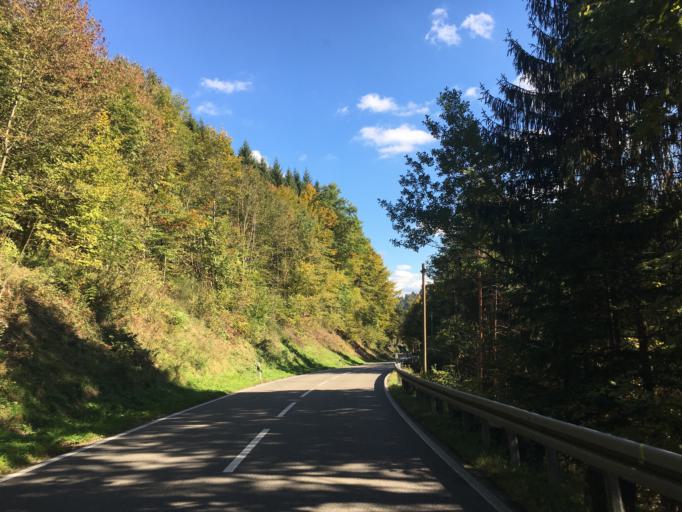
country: DE
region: Baden-Wuerttemberg
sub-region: Karlsruhe Region
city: Oberreichenbach
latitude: 48.7406
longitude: 8.7051
